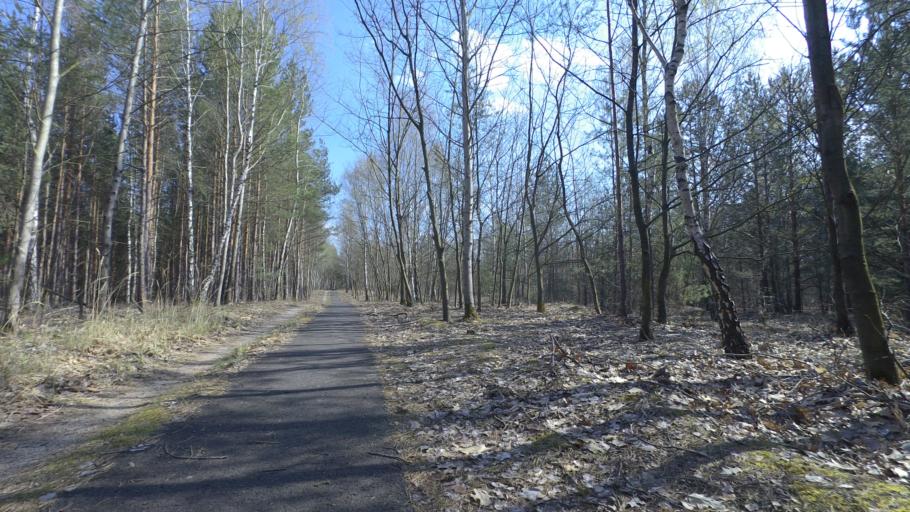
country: DE
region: Brandenburg
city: Mittenwalde
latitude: 52.1828
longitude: 13.5501
